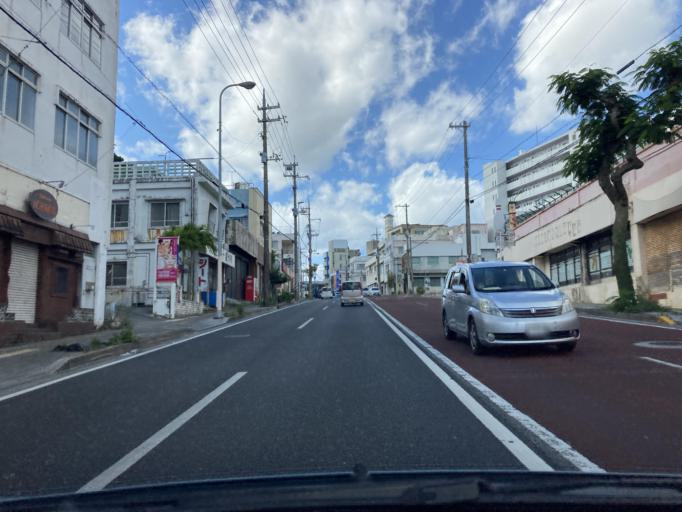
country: JP
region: Okinawa
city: Okinawa
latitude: 26.3377
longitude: 127.8044
